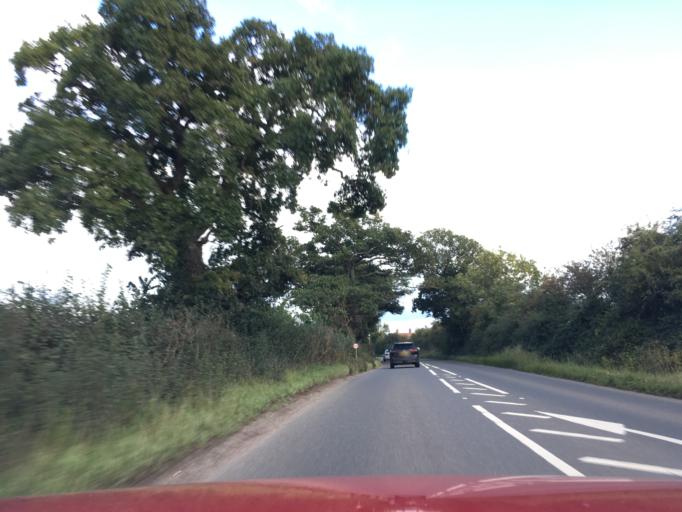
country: GB
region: England
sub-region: Devon
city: Topsham
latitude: 50.7072
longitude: -3.4113
